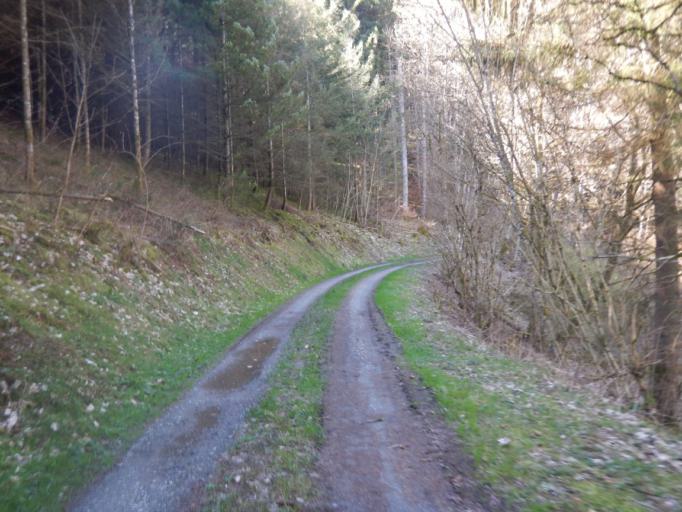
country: LU
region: Diekirch
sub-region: Canton de Wiltz
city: Eschweiler
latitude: 49.9722
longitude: 5.9685
